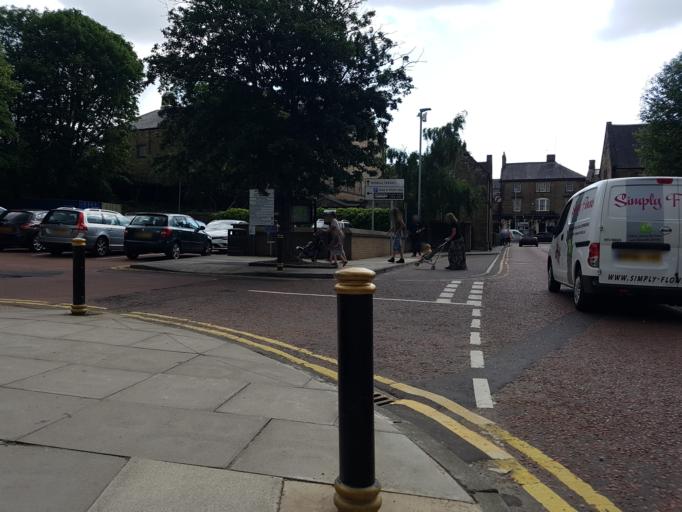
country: GB
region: England
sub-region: Northumberland
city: Alnwick
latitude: 55.4132
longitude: -1.7028
